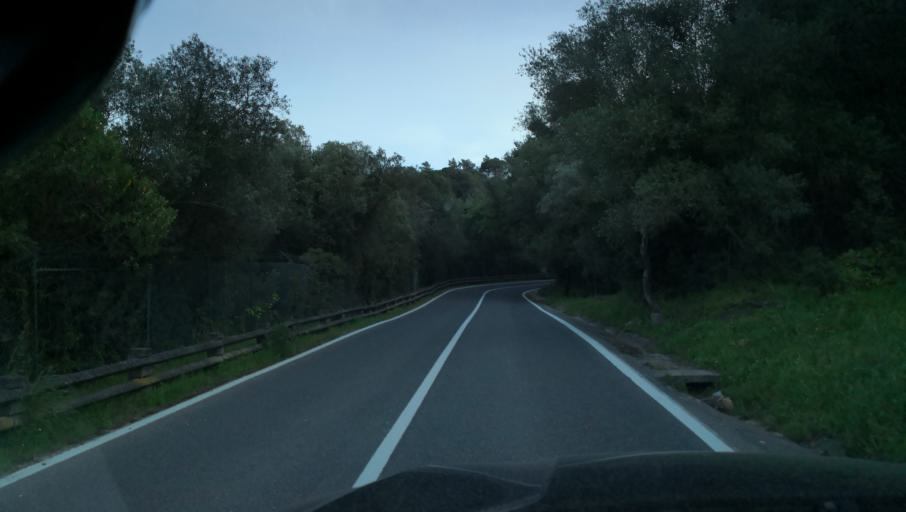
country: PT
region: Setubal
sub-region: Setubal
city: Setubal
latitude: 38.4987
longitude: -8.9376
